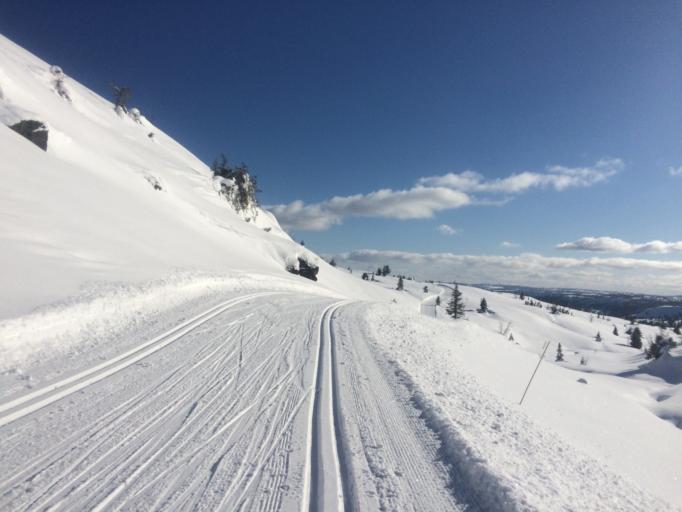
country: NO
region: Oppland
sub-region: Ringebu
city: Ringebu
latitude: 61.3755
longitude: 10.0595
